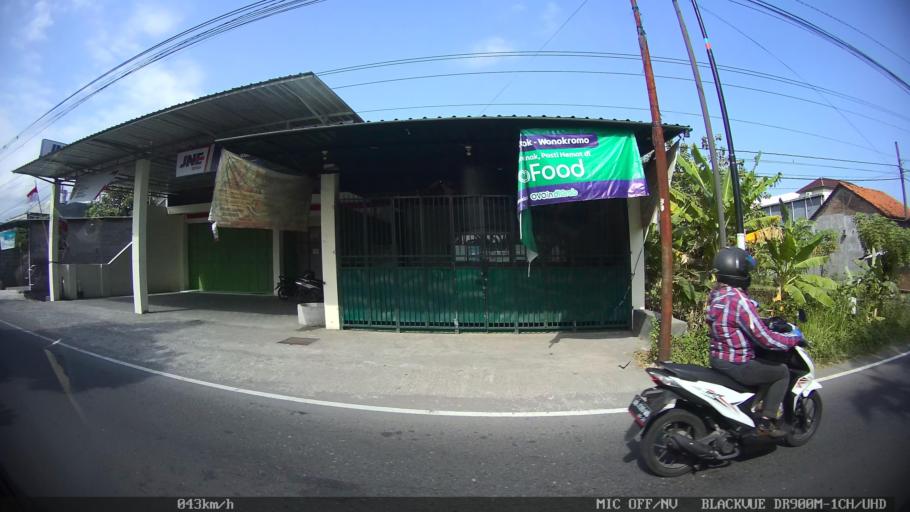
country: ID
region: Daerah Istimewa Yogyakarta
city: Sewon
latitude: -7.8563
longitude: 110.3899
